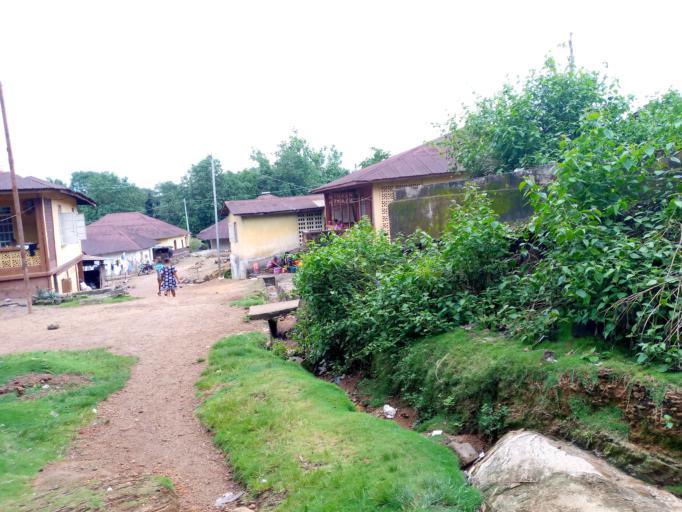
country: SL
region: Northern Province
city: Magburaka
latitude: 8.7246
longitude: -11.9503
